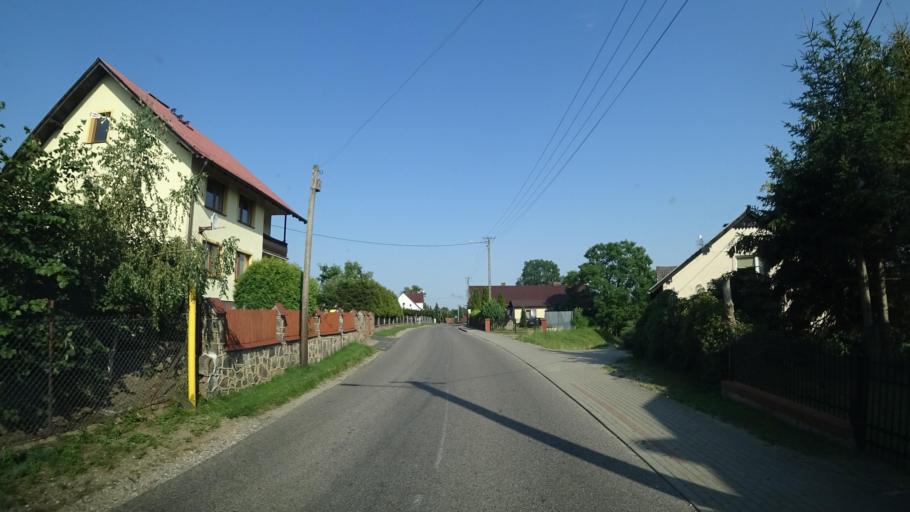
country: PL
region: Pomeranian Voivodeship
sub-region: Powiat czluchowski
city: Rzeczenica
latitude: 53.7573
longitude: 17.1157
